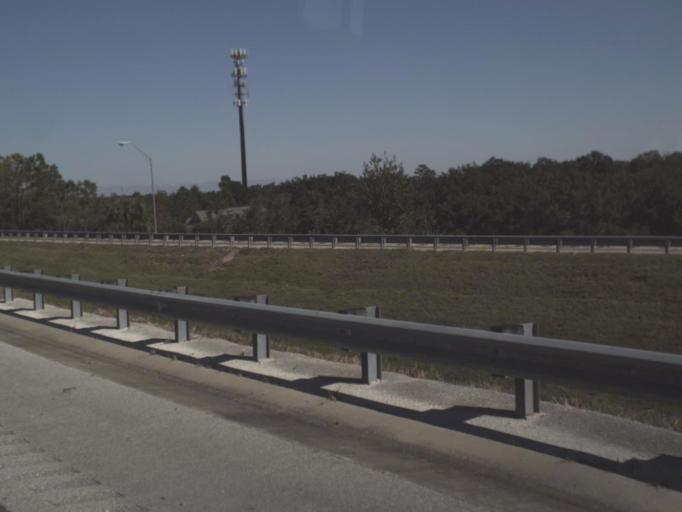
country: US
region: Florida
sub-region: Seminole County
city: Goldenrod
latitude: 28.6223
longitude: -81.2578
